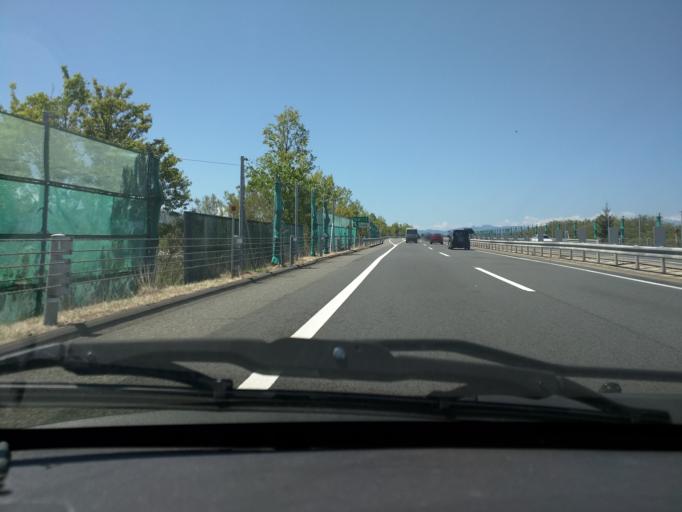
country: JP
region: Nagano
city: Suzaka
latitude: 36.7058
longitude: 138.3051
